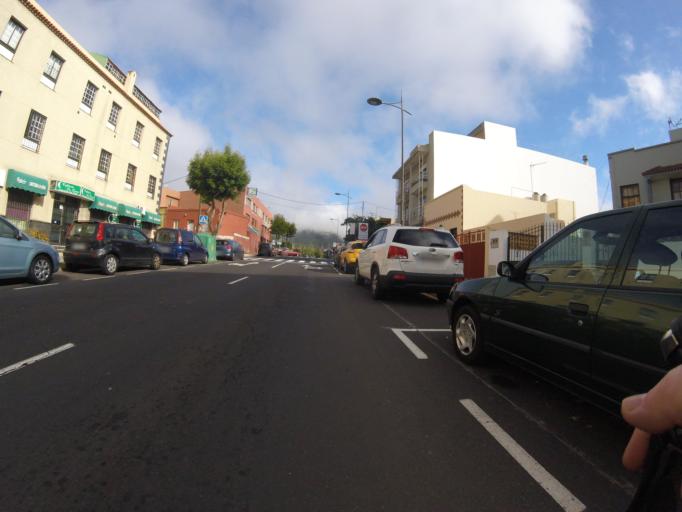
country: ES
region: Canary Islands
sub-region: Provincia de Santa Cruz de Tenerife
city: La Laguna
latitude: 28.4887
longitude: -16.3263
